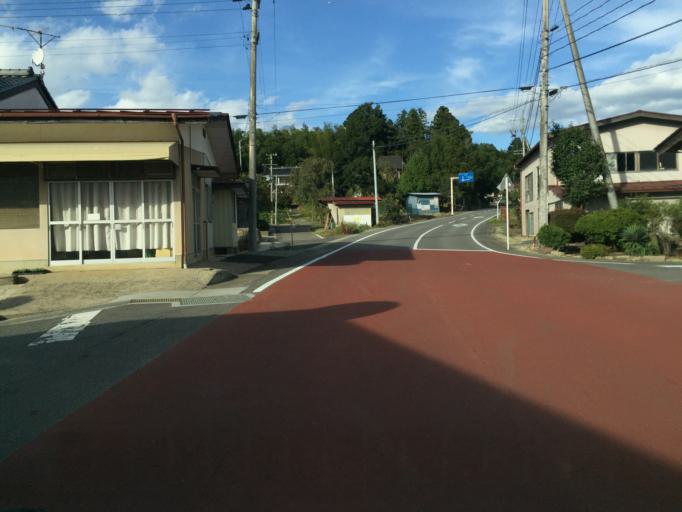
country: JP
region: Fukushima
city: Nihommatsu
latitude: 37.6673
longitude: 140.4234
